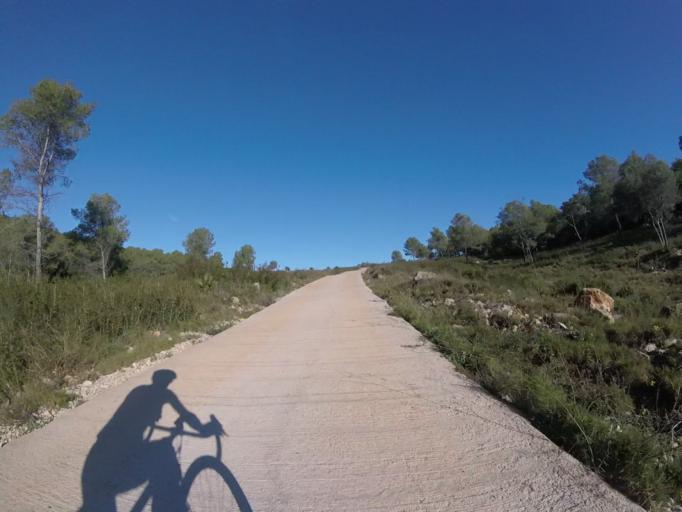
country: ES
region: Valencia
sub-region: Provincia de Castello
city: Santa Magdalena de Pulpis
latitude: 40.3236
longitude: 0.2898
